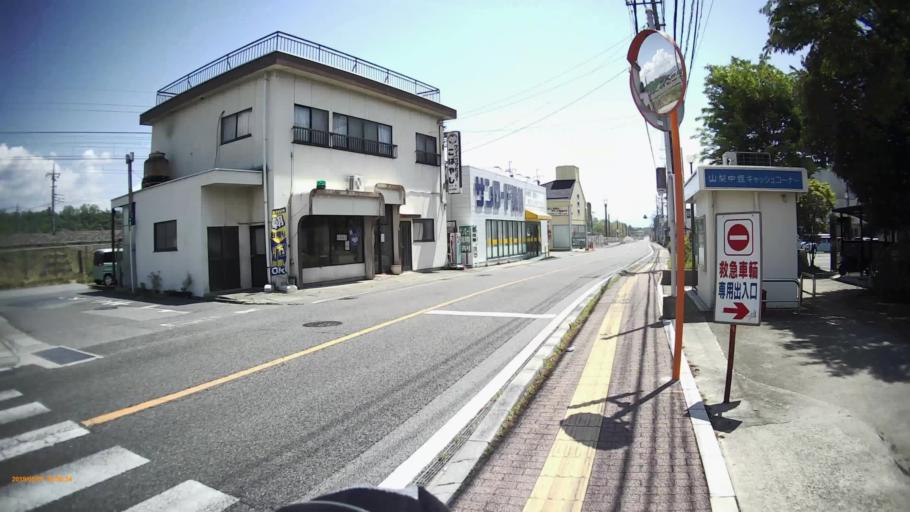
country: JP
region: Yamanashi
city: Nirasaki
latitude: 35.7024
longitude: 138.4574
